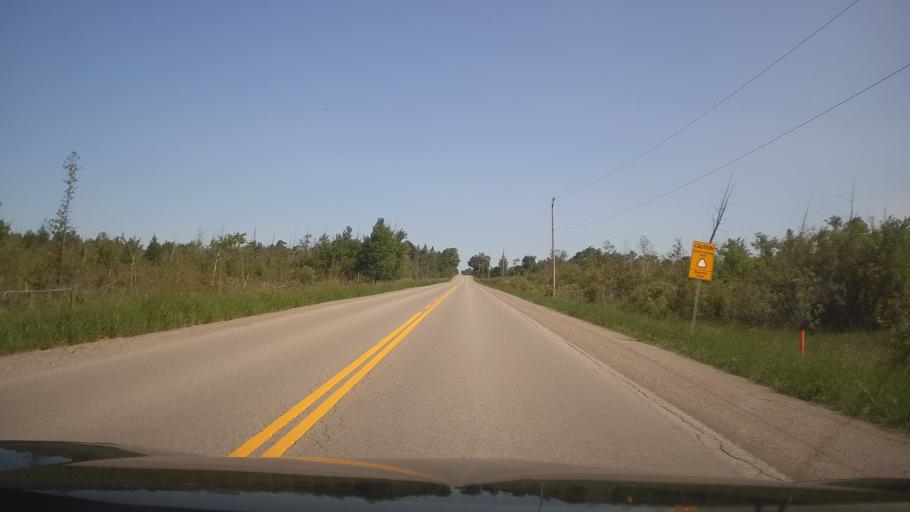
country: CA
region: Ontario
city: Uxbridge
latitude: 44.4725
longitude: -78.9370
